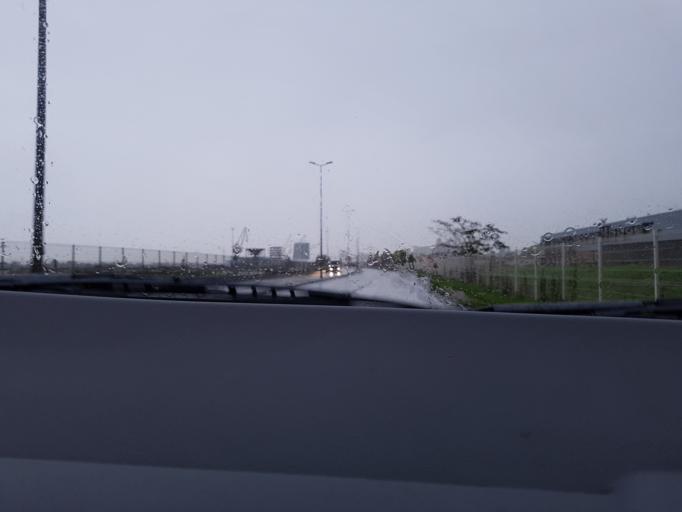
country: FR
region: Aquitaine
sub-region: Departement de la Gironde
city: Bassens
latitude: 44.9005
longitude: -0.5326
